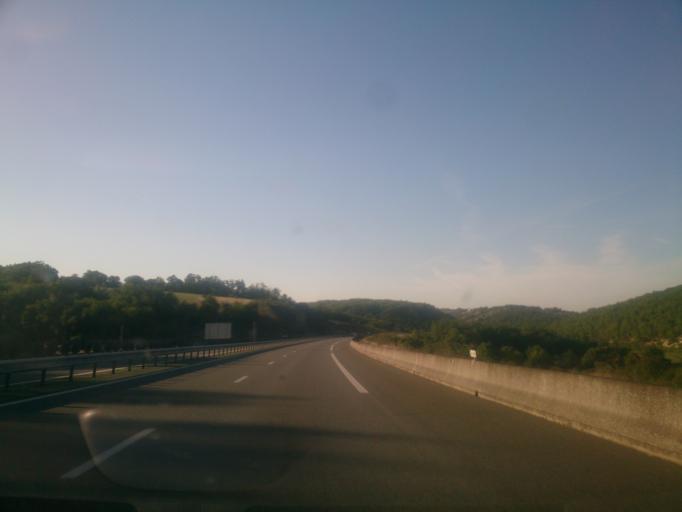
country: FR
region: Midi-Pyrenees
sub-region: Departement du Lot
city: Le Vigan
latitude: 44.7256
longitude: 1.5590
